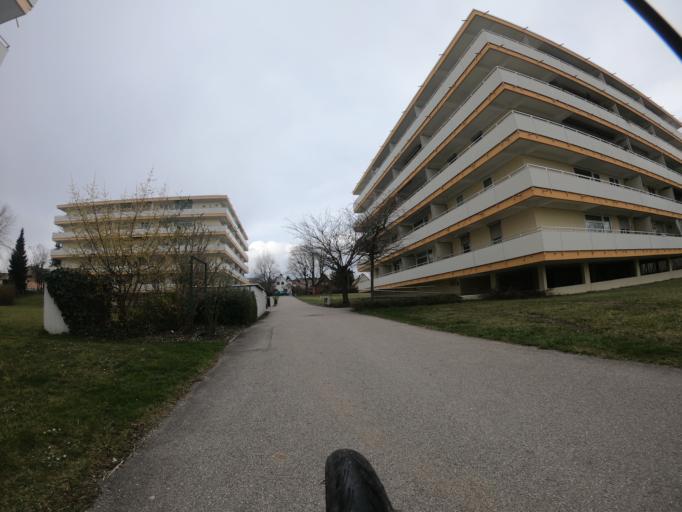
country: DE
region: Bavaria
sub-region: Upper Bavaria
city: Fuerstenfeldbruck
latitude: 48.1821
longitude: 11.2505
